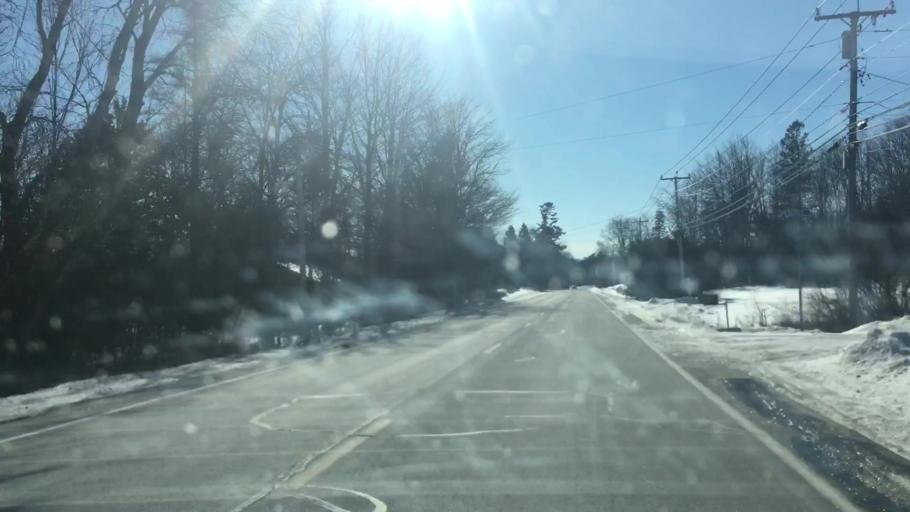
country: US
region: Maine
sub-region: Hancock County
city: Ellsworth
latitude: 44.5014
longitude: -68.4419
